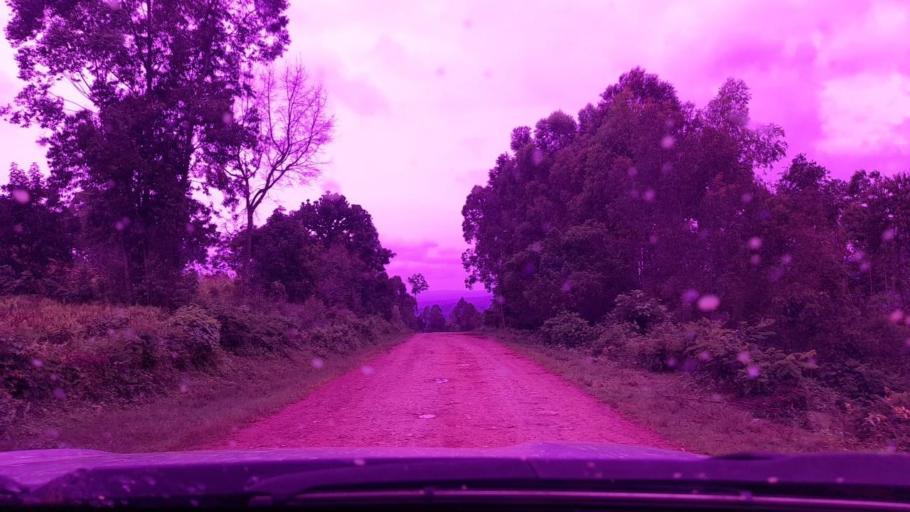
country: ET
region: Southern Nations, Nationalities, and People's Region
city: Bonga
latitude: 7.5516
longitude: 35.8432
